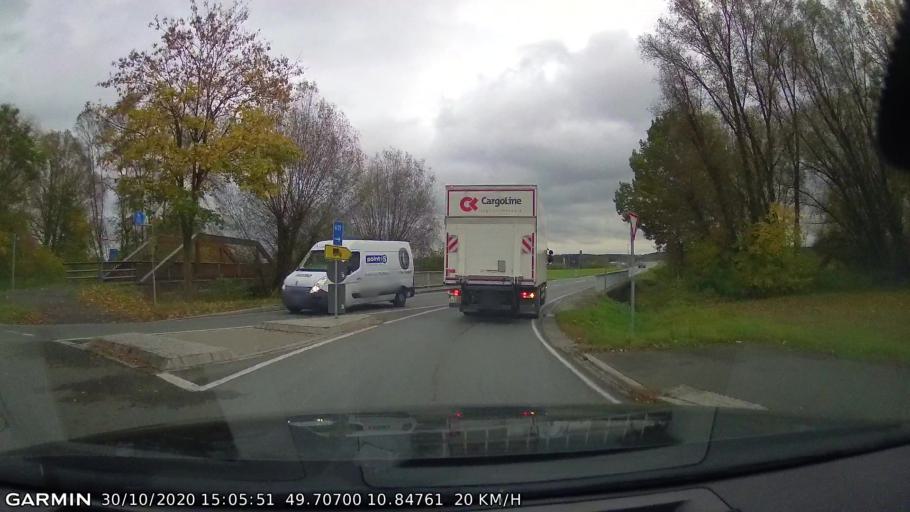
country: DE
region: Bavaria
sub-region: Regierungsbezirk Mittelfranken
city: Gremsdorf
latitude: 49.7070
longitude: 10.8476
